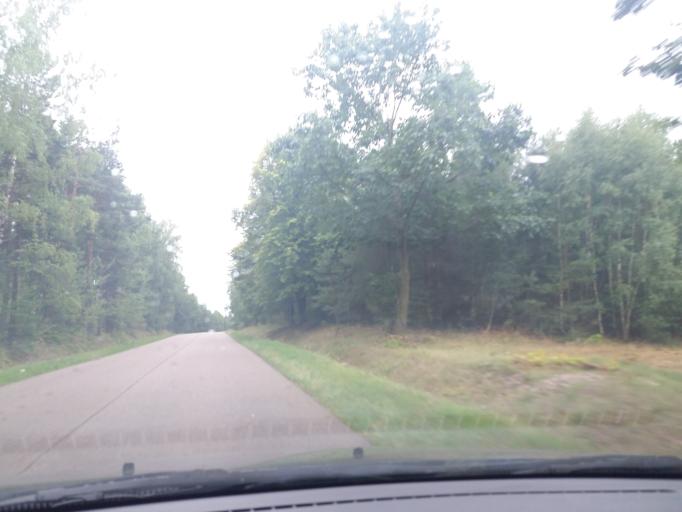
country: PL
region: Masovian Voivodeship
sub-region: Powiat mlawski
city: Wieczfnia Koscielna
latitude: 53.2092
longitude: 20.5016
